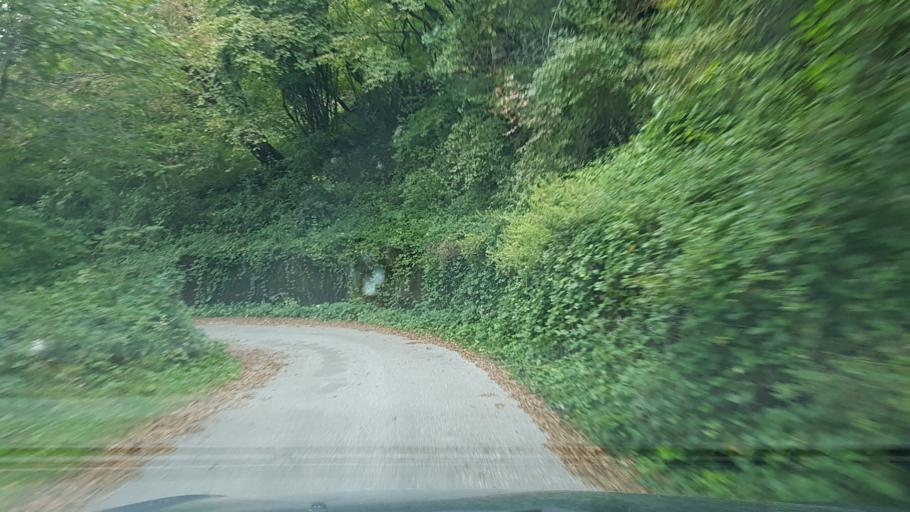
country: IT
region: Friuli Venezia Giulia
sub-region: Provincia di Udine
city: Venzone
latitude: 46.3356
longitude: 13.1691
